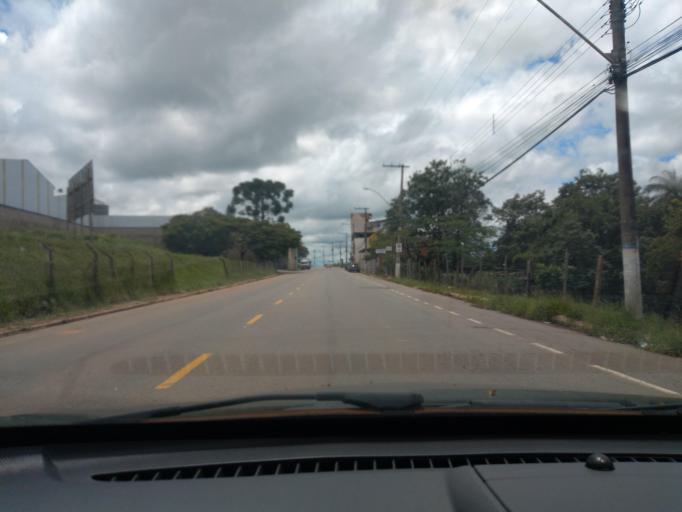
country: BR
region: Minas Gerais
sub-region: Lavras
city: Lavras
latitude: -21.2429
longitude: -45.0215
